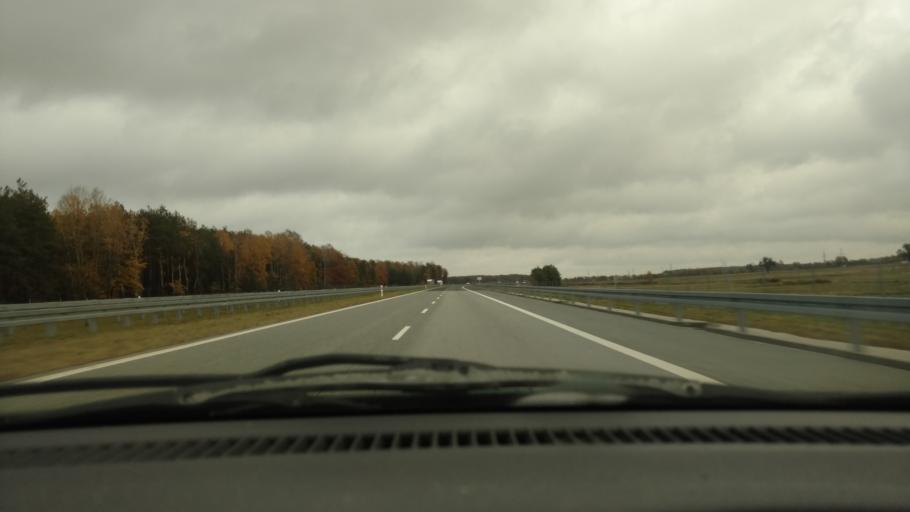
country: PL
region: Lodz Voivodeship
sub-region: Powiat pabianicki
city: Dobron
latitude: 51.6029
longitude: 19.2898
